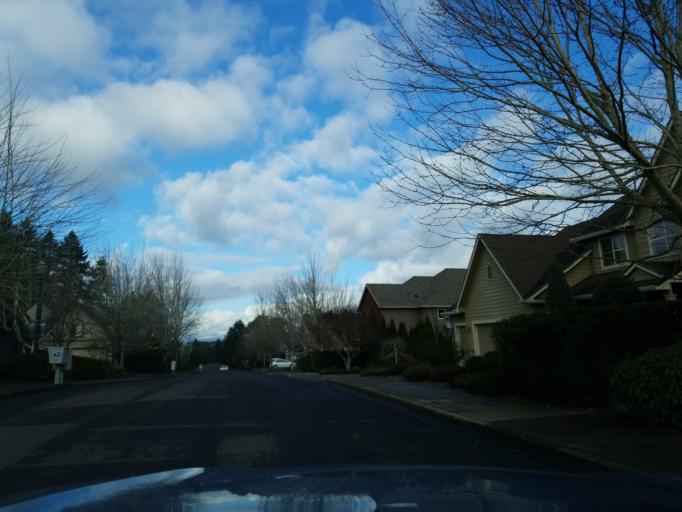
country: US
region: Washington
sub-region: Clark County
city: Felida
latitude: 45.7146
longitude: -122.7048
